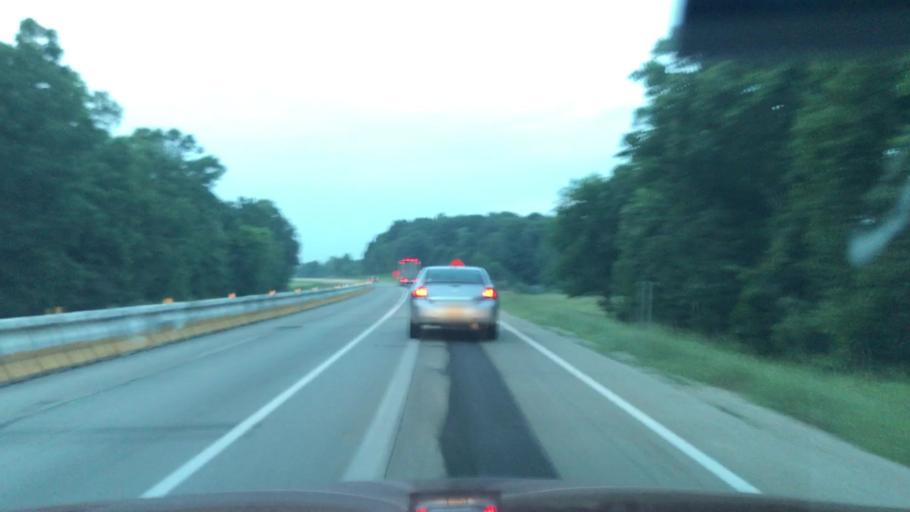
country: US
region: Michigan
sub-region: Kent County
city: Rockford
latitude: 43.1349
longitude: -85.5917
